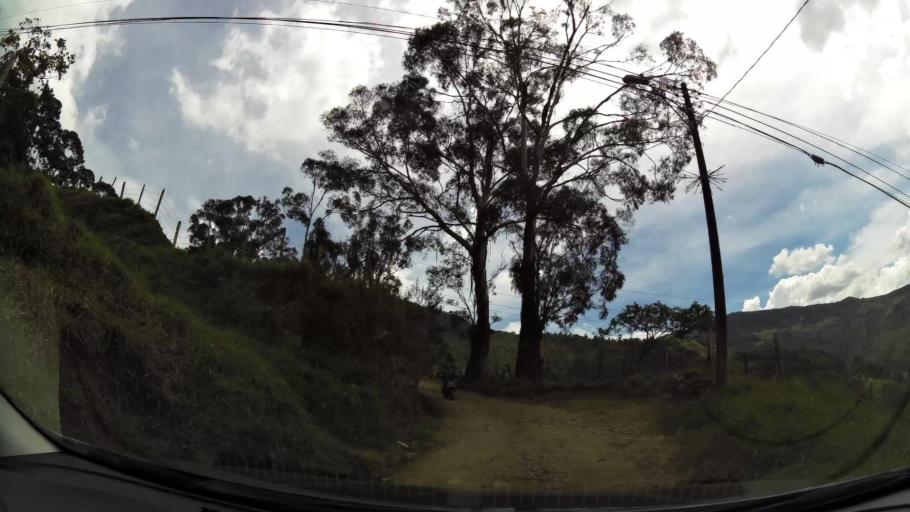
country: CO
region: Antioquia
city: Municipio de Copacabana
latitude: 6.3221
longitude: -75.4927
